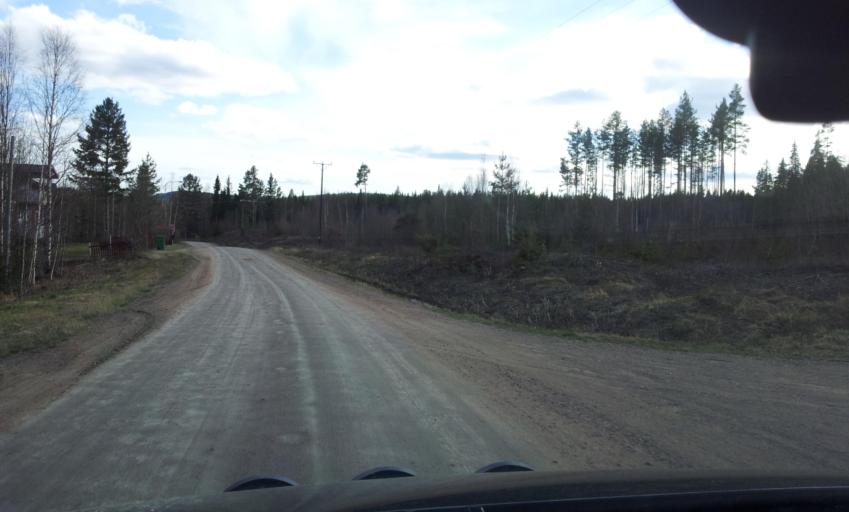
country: SE
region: Vaesternorrland
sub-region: Ange Kommun
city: Ange
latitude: 62.1528
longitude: 15.6612
